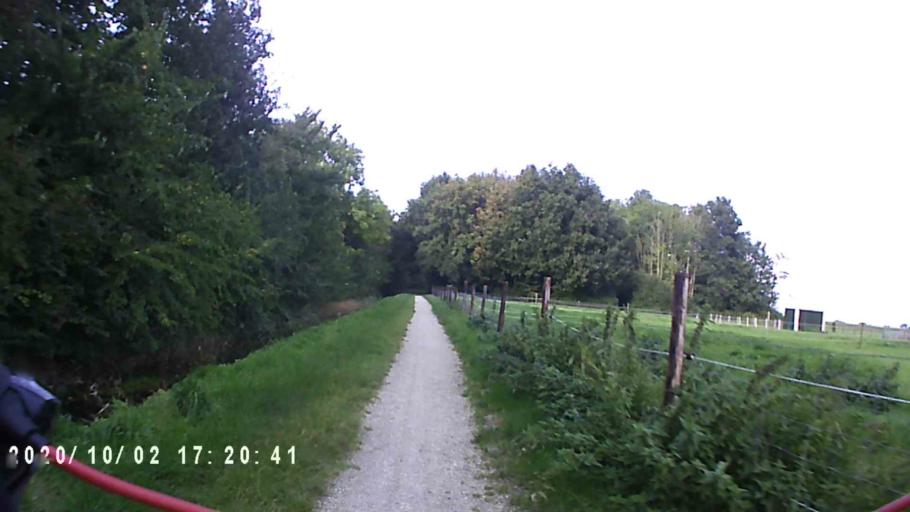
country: NL
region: Groningen
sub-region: Gemeente De Marne
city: Ulrum
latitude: 53.3397
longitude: 6.3084
